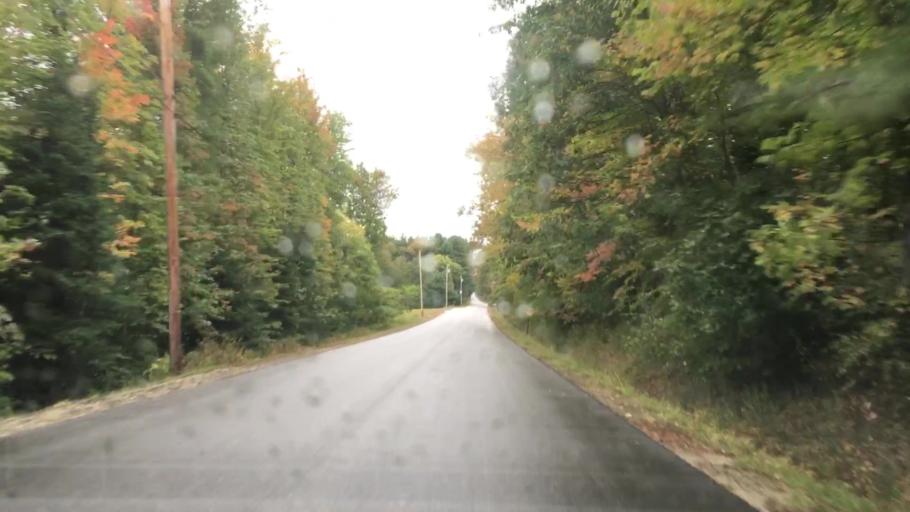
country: US
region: Maine
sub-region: Cumberland County
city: Harrison
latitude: 44.0848
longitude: -70.6478
